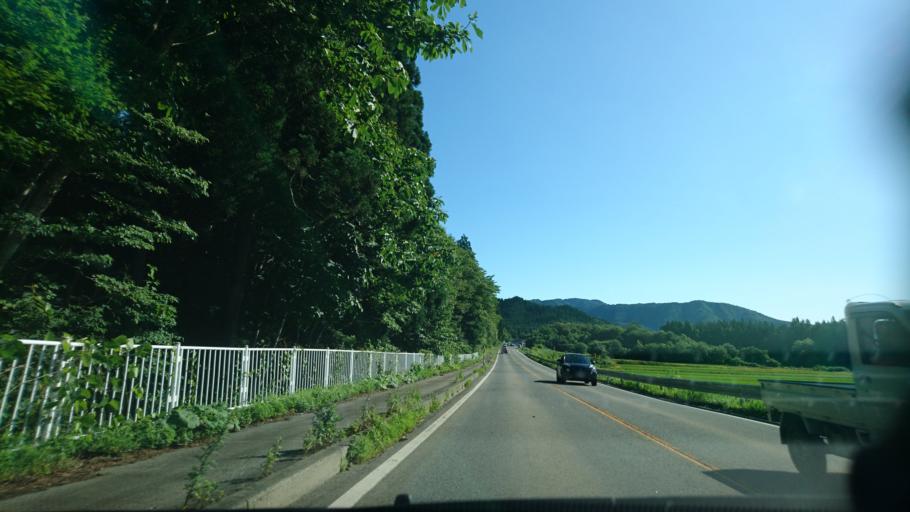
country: JP
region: Akita
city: Kakunodatemachi
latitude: 39.6153
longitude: 140.4382
